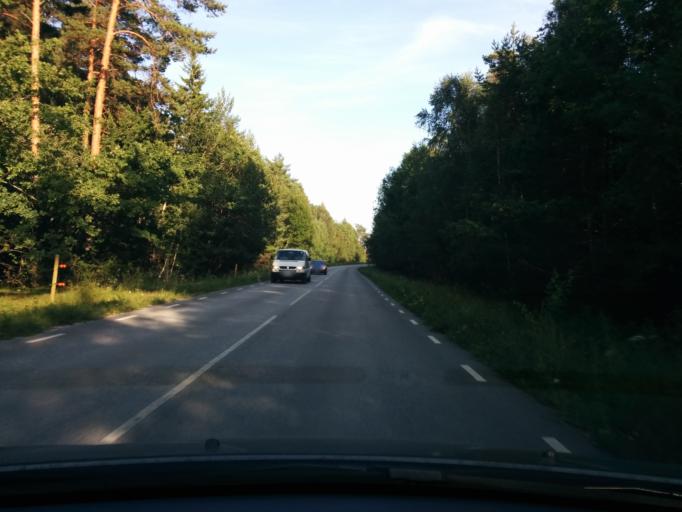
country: SE
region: Gotland
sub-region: Gotland
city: Visby
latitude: 57.5197
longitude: 18.5472
